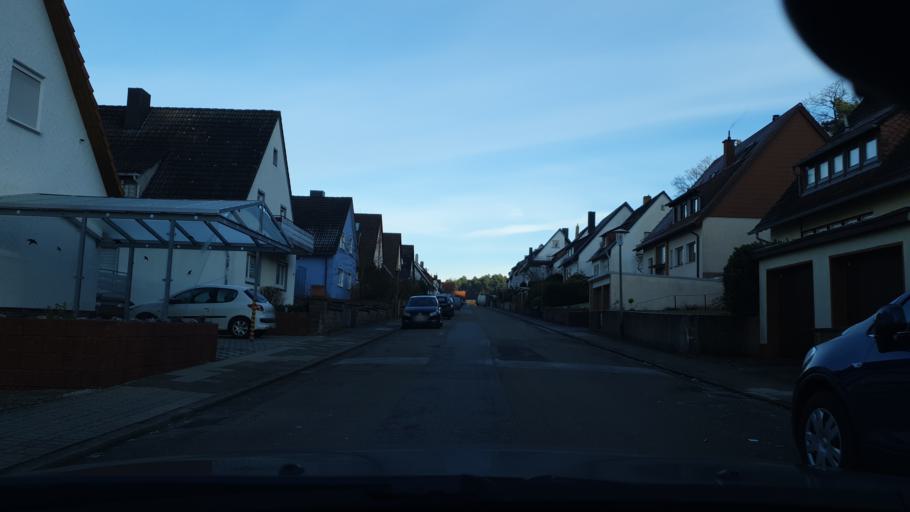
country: DE
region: Rheinland-Pfalz
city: Kaiserslautern
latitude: 49.4364
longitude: 7.7268
